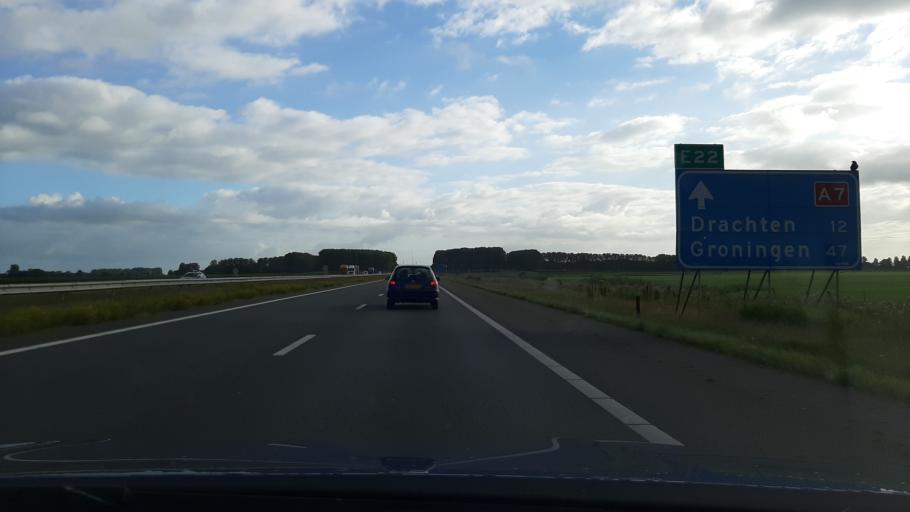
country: NL
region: Friesland
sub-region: Gemeente Opsterland
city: Tijnje
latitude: 53.0130
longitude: 6.0032
